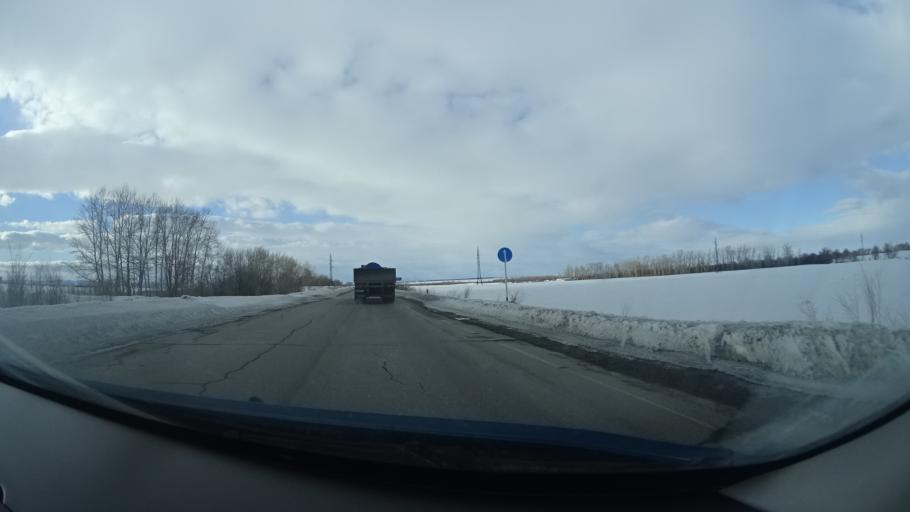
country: RU
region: Chelyabinsk
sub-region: Gorod Magnitogorsk
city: Magnitogorsk
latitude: 53.5832
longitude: 58.8845
